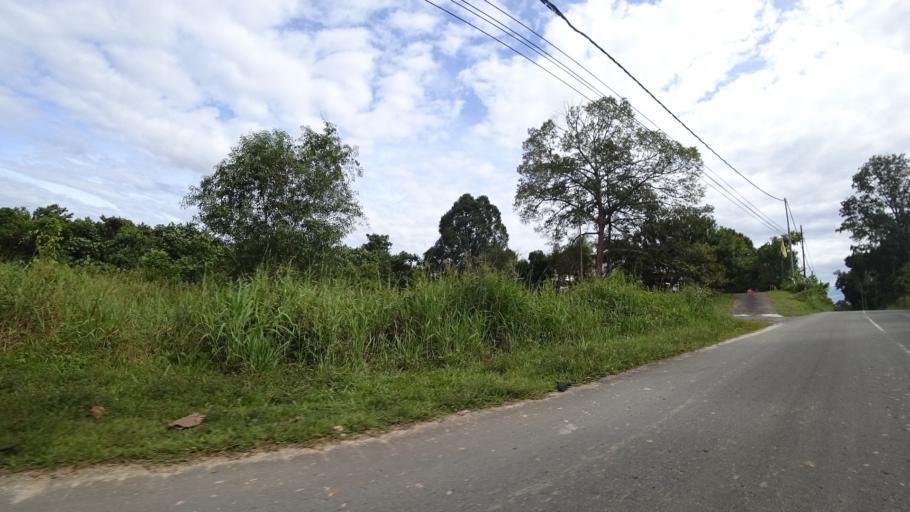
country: MY
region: Sarawak
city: Limbang
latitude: 4.8349
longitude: 114.9492
